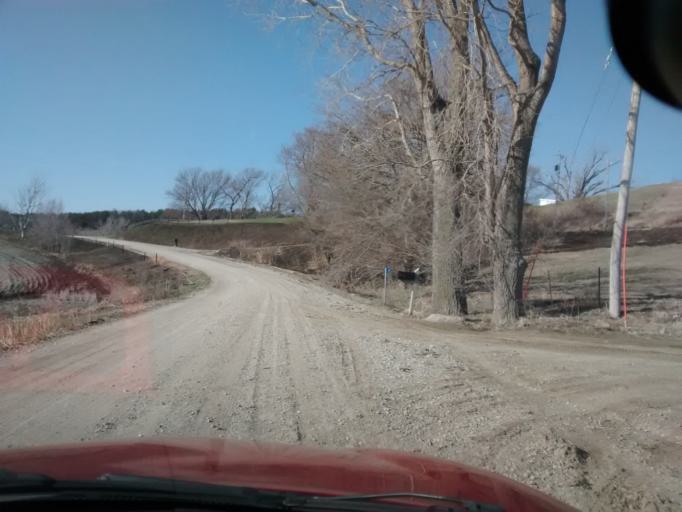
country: US
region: Iowa
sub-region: Pottawattamie County
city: Carter Lake
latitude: 41.4055
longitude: -95.8498
